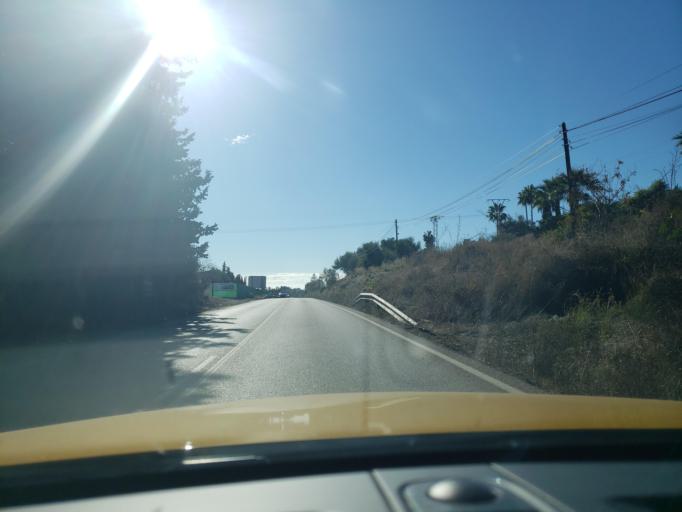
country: ES
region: Andalusia
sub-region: Provincia de Malaga
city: Benahavis
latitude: 36.4781
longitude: -5.0137
